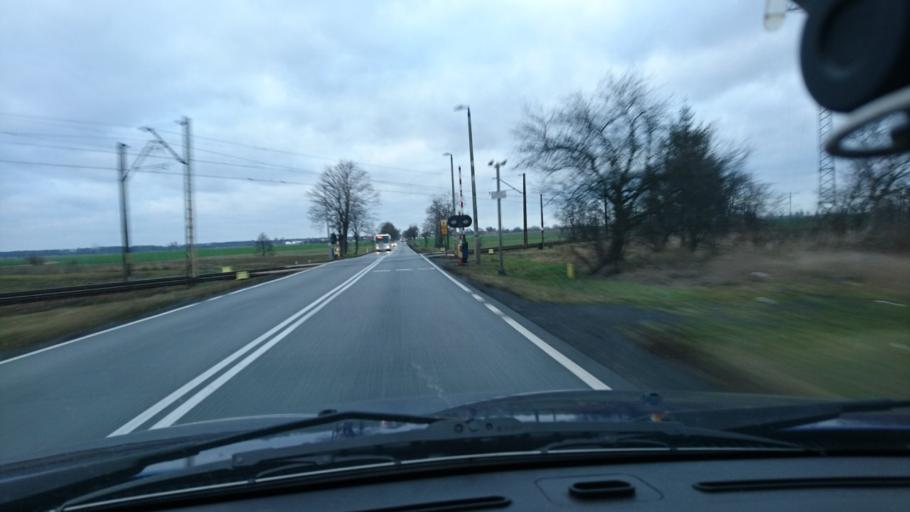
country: PL
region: Opole Voivodeship
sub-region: Powiat kluczborski
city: Kluczbork
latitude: 51.0156
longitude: 18.2002
